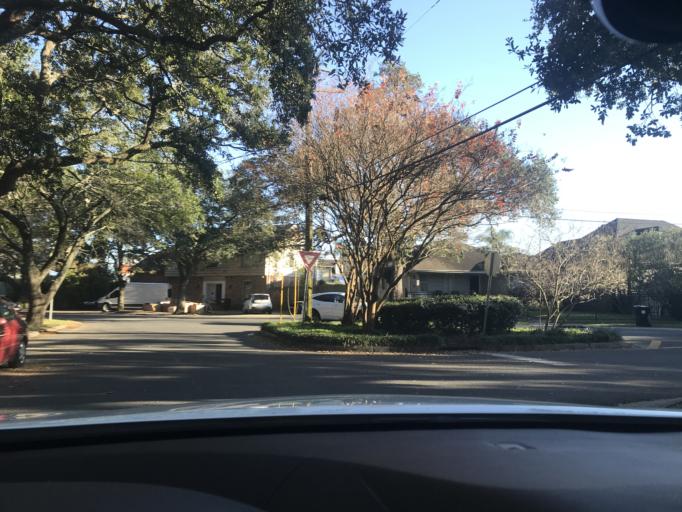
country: US
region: Louisiana
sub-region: Orleans Parish
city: New Orleans
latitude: 29.9561
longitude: -90.1069
